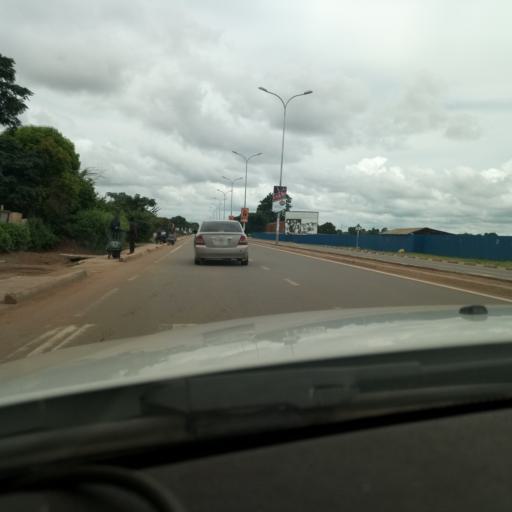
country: ZM
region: Lusaka
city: Lusaka
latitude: -15.4430
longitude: 28.3167
